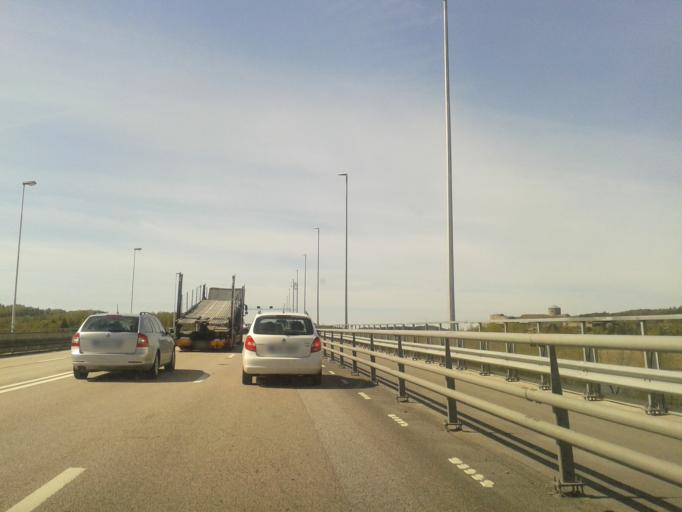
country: SE
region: Vaestra Goetaland
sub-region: Ale Kommun
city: Surte
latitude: 57.8546
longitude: 12.0127
